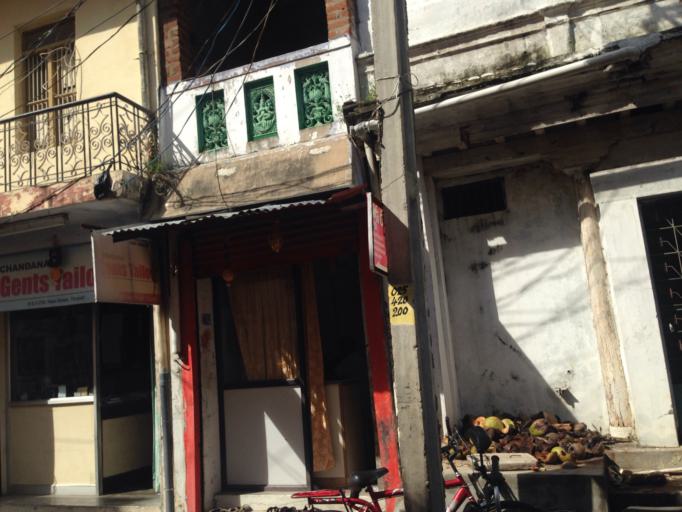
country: IN
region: Andhra Pradesh
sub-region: Chittoor
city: Tirupati
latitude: 13.6335
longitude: 79.4160
